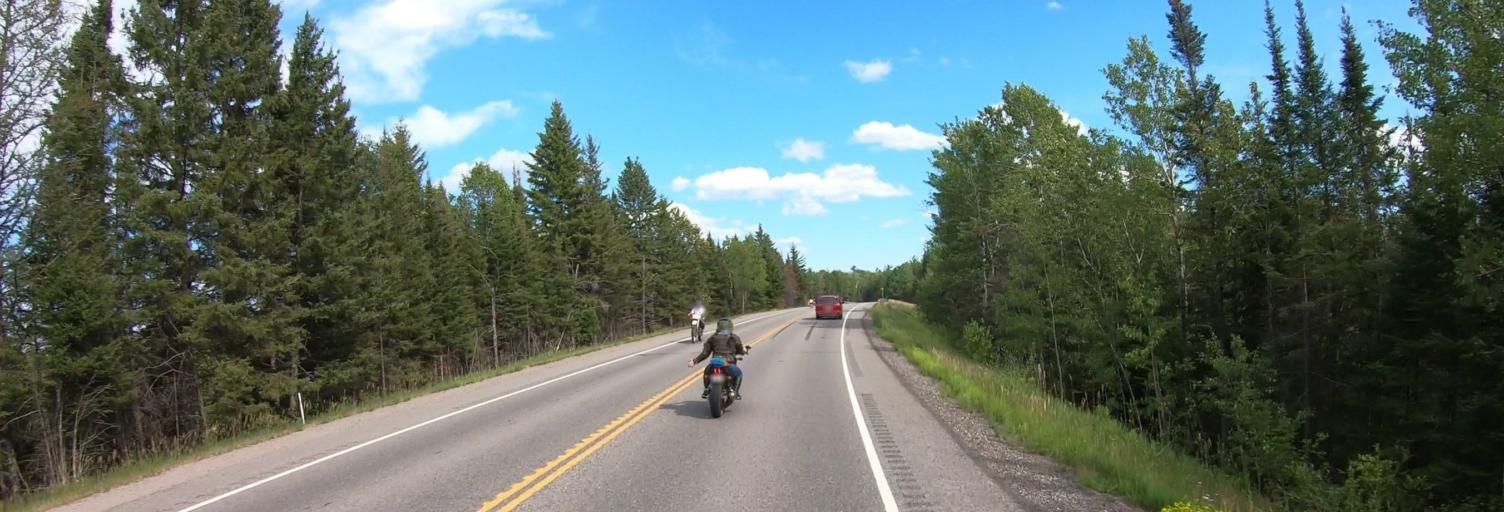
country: US
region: Minnesota
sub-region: Saint Louis County
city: Ely
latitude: 47.8819
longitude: -91.9833
